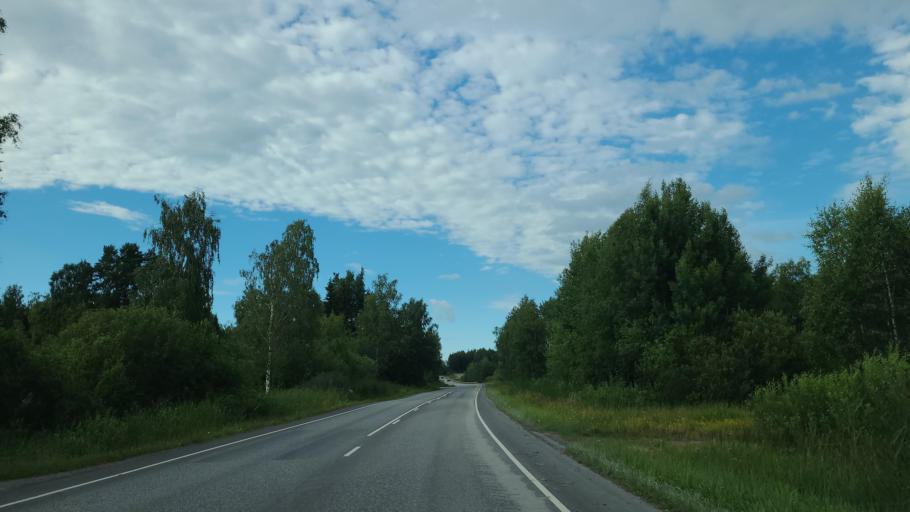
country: FI
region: Varsinais-Suomi
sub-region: Turku
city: Merimasku
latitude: 60.4307
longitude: 21.8947
